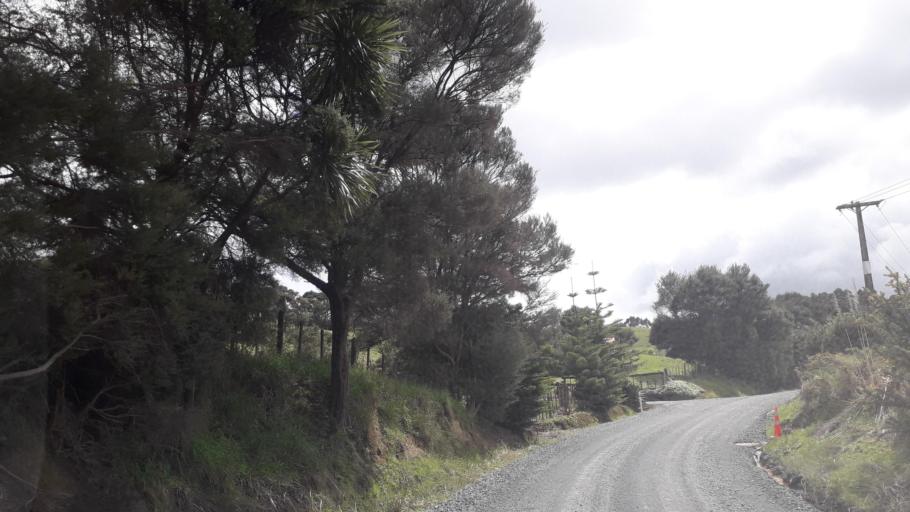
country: NZ
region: Northland
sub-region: Far North District
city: Kaitaia
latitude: -35.1595
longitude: 173.3418
